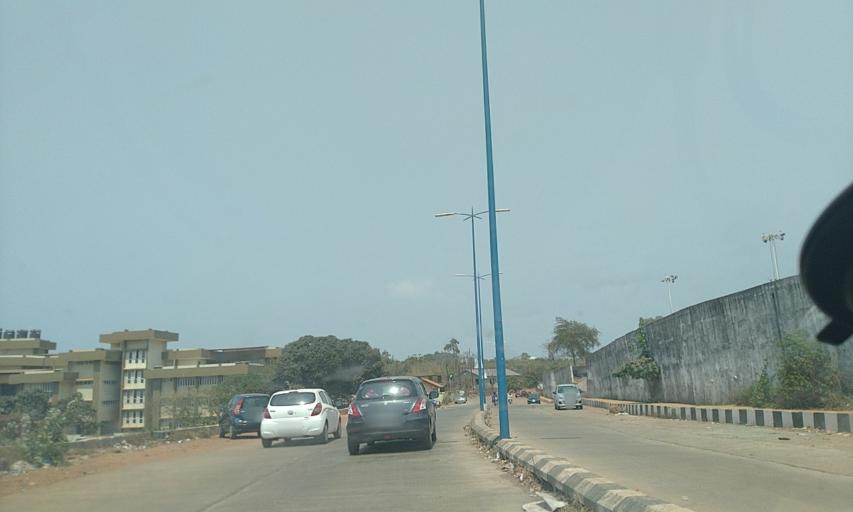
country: IN
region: Goa
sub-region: North Goa
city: Bambolim
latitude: 15.4687
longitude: 73.8618
